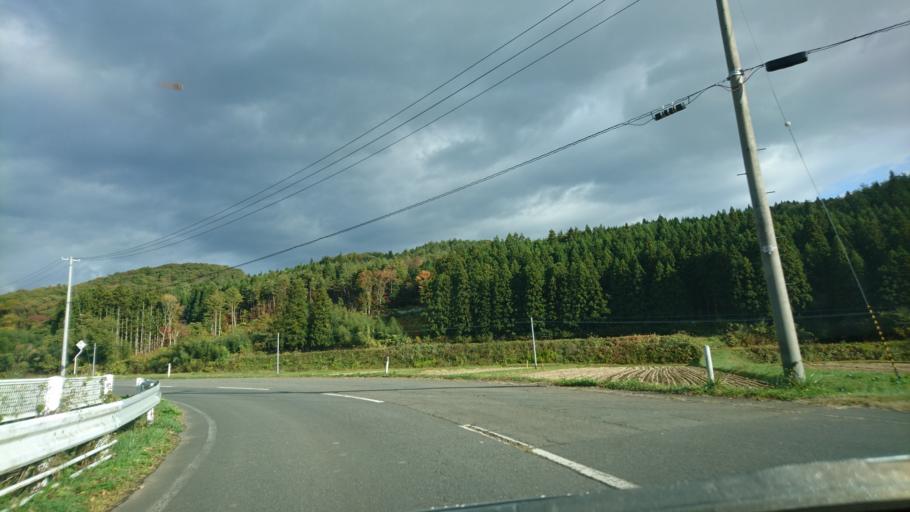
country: JP
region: Iwate
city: Mizusawa
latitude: 39.0850
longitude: 140.9904
